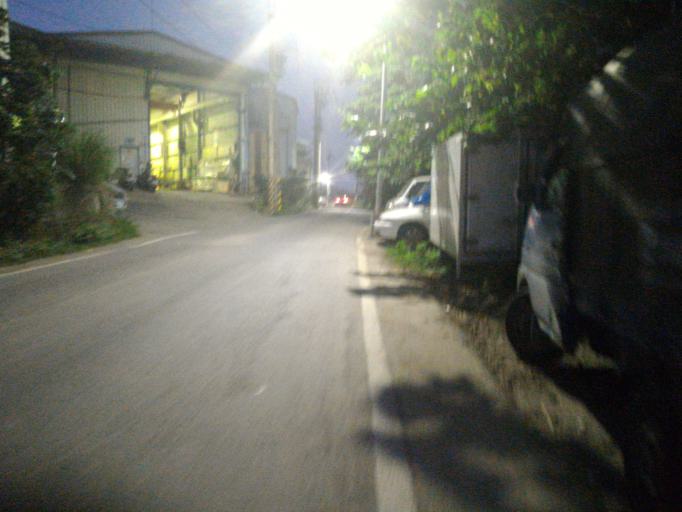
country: TW
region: Taipei
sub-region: Taipei
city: Banqiao
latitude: 24.9611
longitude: 121.4092
